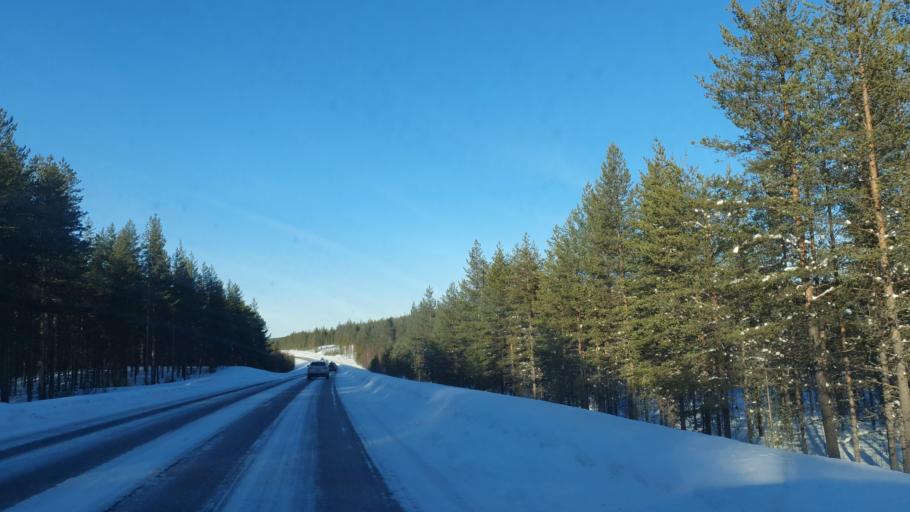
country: FI
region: Lapland
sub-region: Torniolaakso
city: Pello
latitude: 66.9247
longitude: 24.0867
